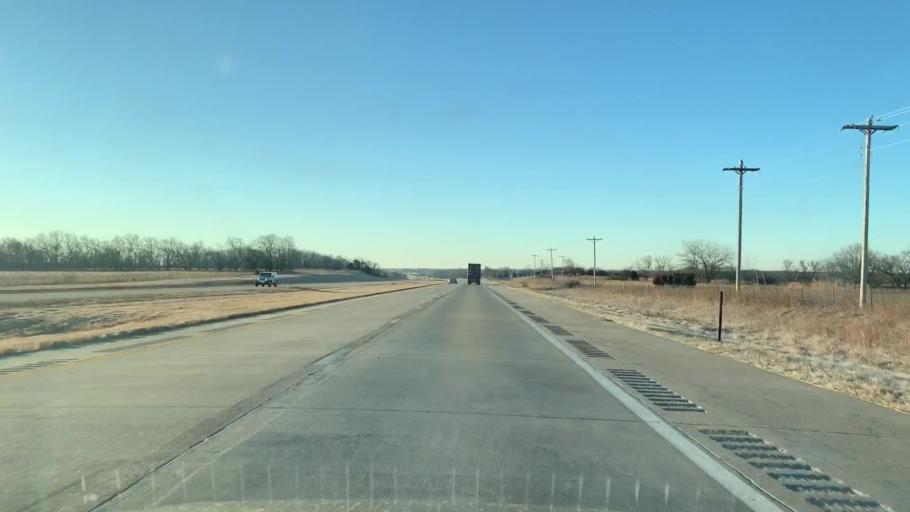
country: US
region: Kansas
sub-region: Linn County
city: Pleasanton
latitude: 38.0905
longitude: -94.7136
